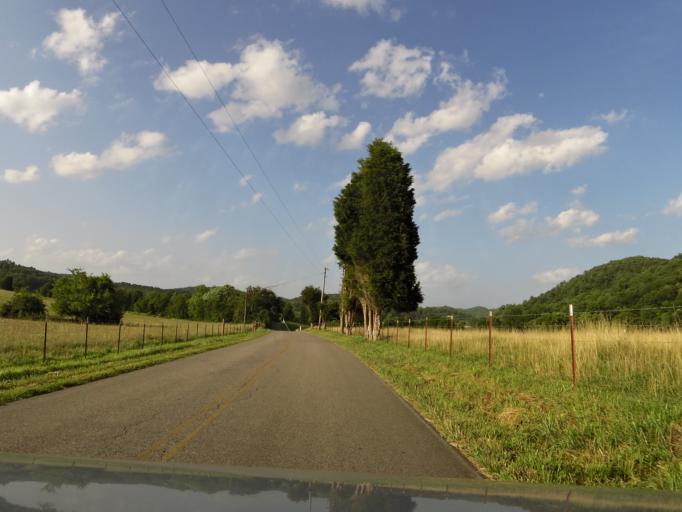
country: US
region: Tennessee
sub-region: Blount County
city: Wildwood
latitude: 35.8334
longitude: -83.8742
